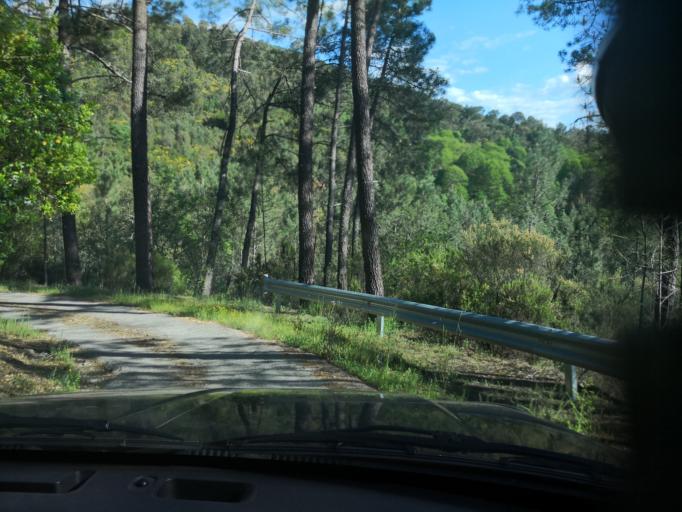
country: PT
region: Vila Real
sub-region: Vila Real
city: Vila Real
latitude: 41.2731
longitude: -7.7488
